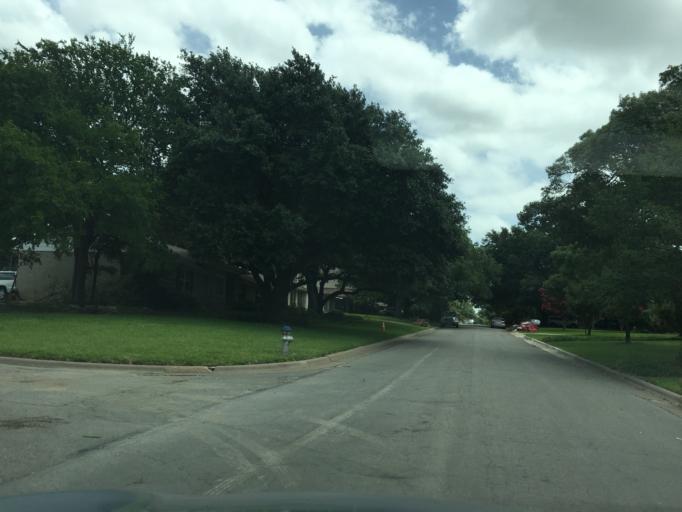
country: US
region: Texas
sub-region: Dallas County
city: University Park
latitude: 32.8974
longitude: -96.7899
